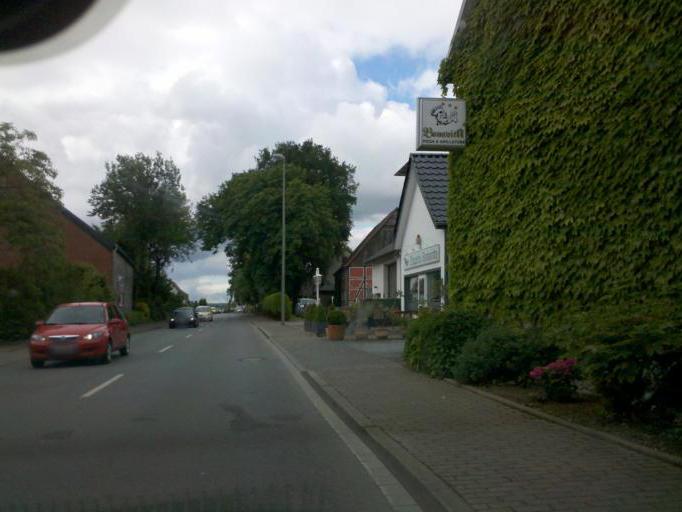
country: DE
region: North Rhine-Westphalia
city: Erwitte
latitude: 51.6208
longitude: 8.3077
